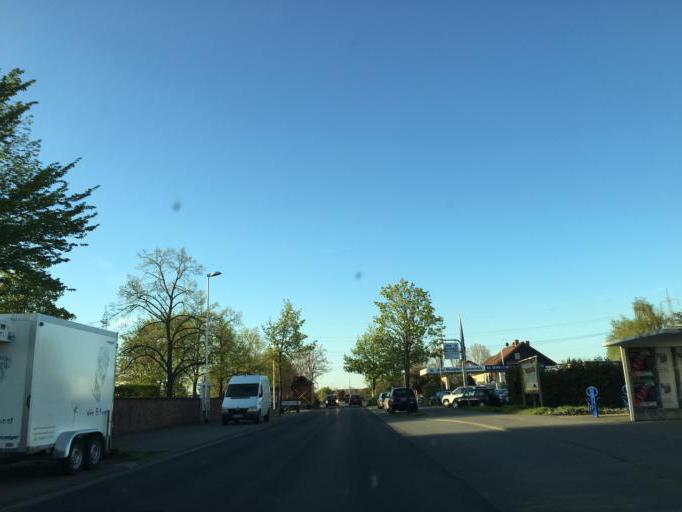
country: DE
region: Hesse
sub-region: Regierungsbezirk Darmstadt
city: Rodgau
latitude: 50.0123
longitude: 8.8903
